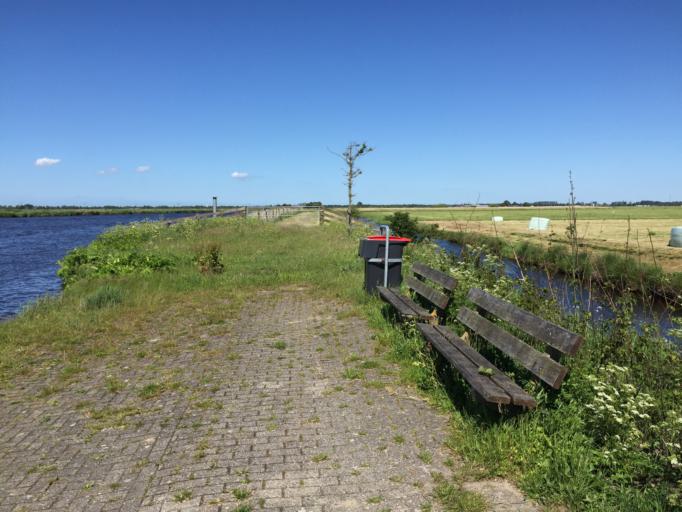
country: NL
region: Friesland
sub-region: Gemeente Tytsjerksteradiel
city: Garyp
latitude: 53.1725
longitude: 5.9381
